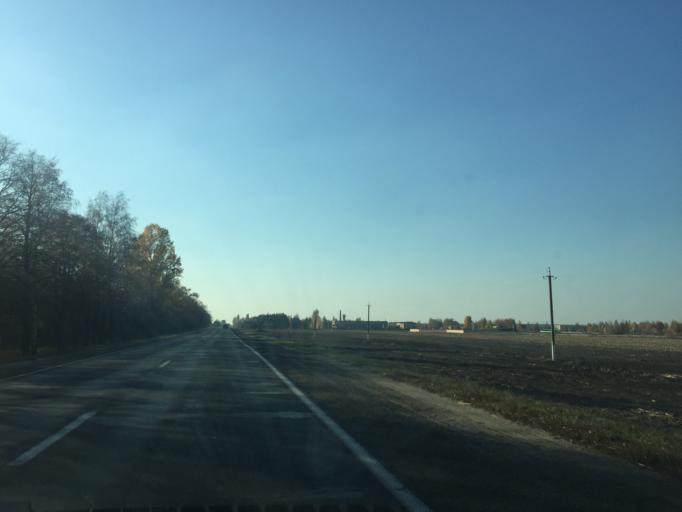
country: BY
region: Gomel
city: Dobrush
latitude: 52.3837
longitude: 31.3641
